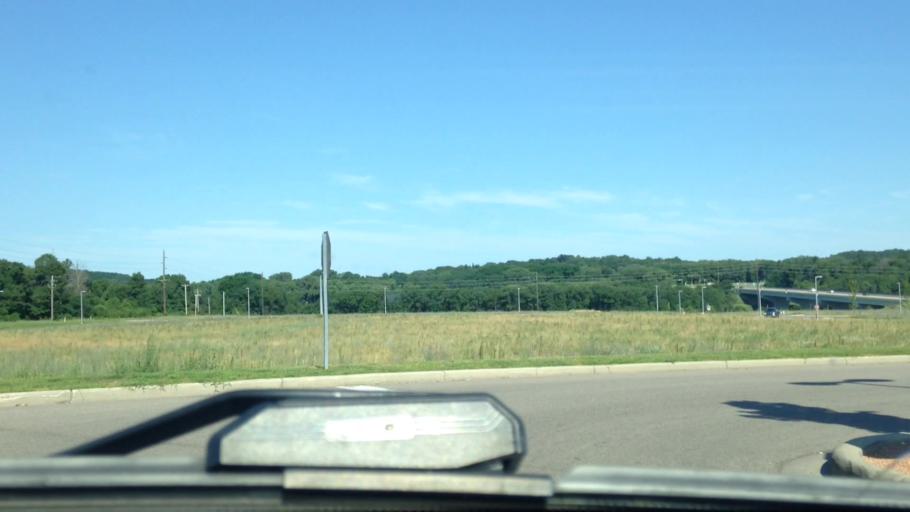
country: US
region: Wisconsin
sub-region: Eau Claire County
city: Altoona
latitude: 44.8164
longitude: -91.4588
